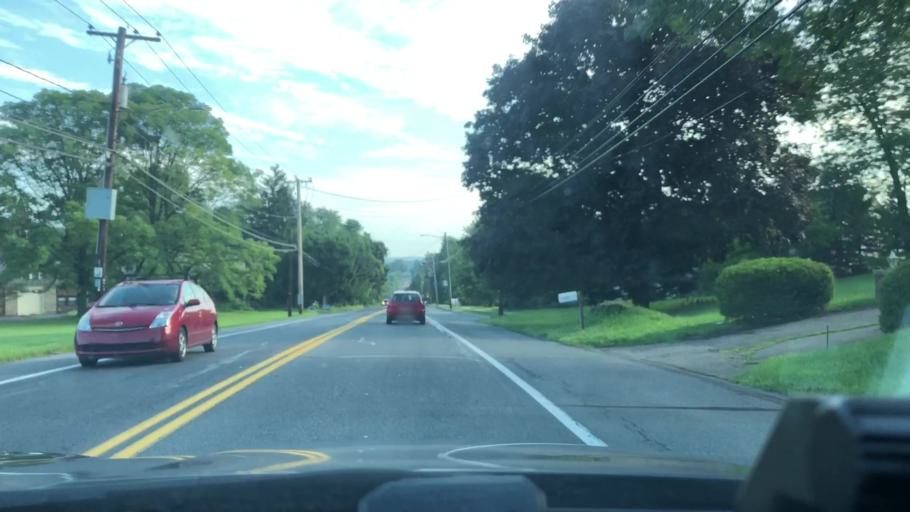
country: US
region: Pennsylvania
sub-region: Northampton County
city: Middletown
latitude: 40.6623
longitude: -75.3523
